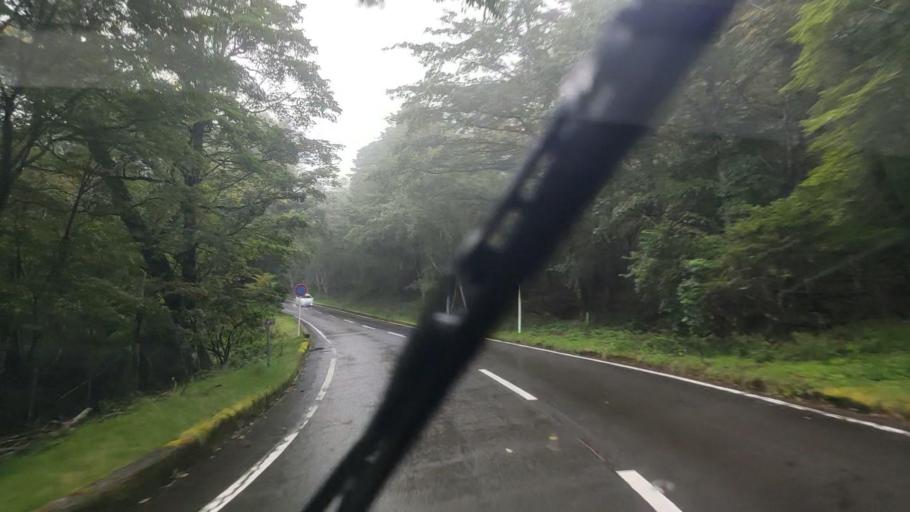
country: JP
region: Shizuoka
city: Fuji
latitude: 35.3119
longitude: 138.7417
